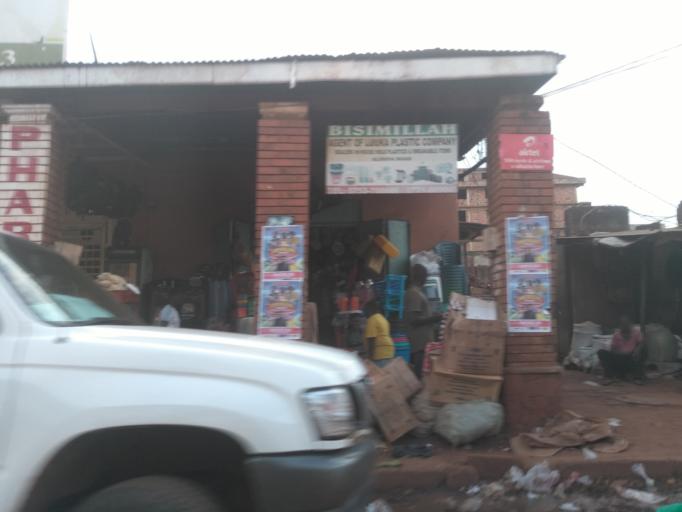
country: UG
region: Eastern Region
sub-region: Jinja District
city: Jinja
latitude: 0.4319
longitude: 33.2130
